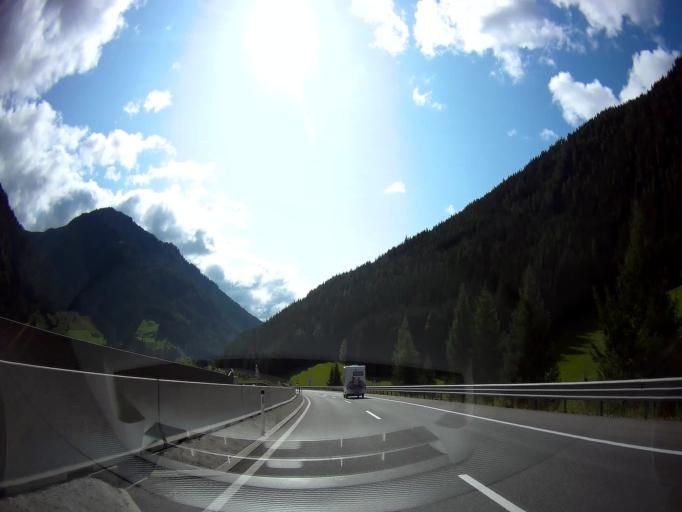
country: AT
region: Salzburg
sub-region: Politischer Bezirk Tamsweg
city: Zederhaus
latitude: 47.1564
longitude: 13.4920
